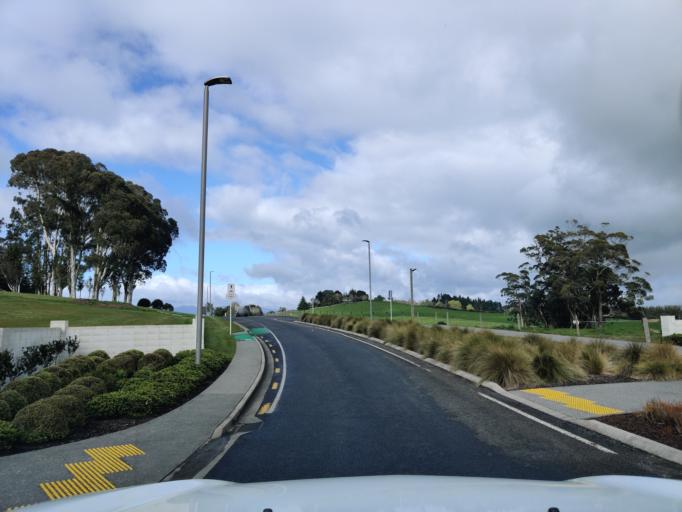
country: NZ
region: Waikato
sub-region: Hamilton City
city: Hamilton
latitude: -37.8251
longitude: 175.2242
